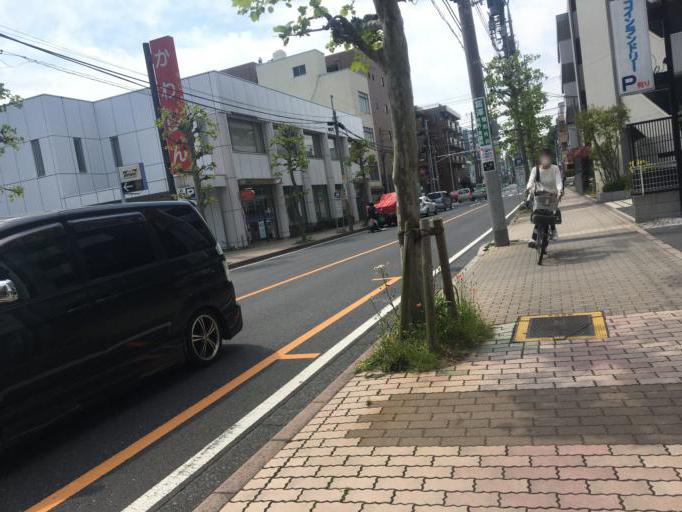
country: JP
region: Saitama
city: Wako
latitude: 35.7849
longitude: 139.6095
